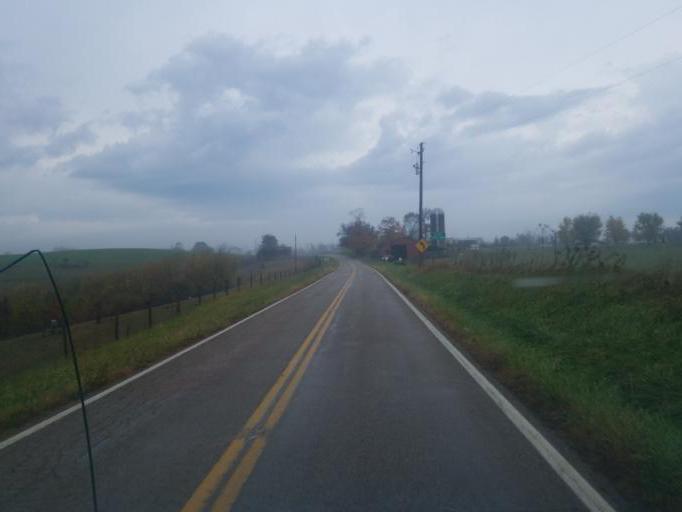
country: US
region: Ohio
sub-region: Athens County
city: Glouster
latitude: 39.5266
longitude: -81.9394
